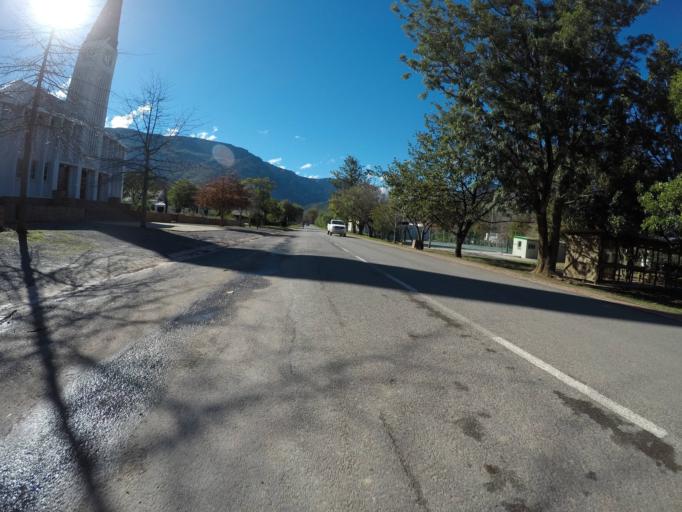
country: ZA
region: Western Cape
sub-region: Overberg District Municipality
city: Caledon
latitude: -34.0489
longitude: 19.6096
